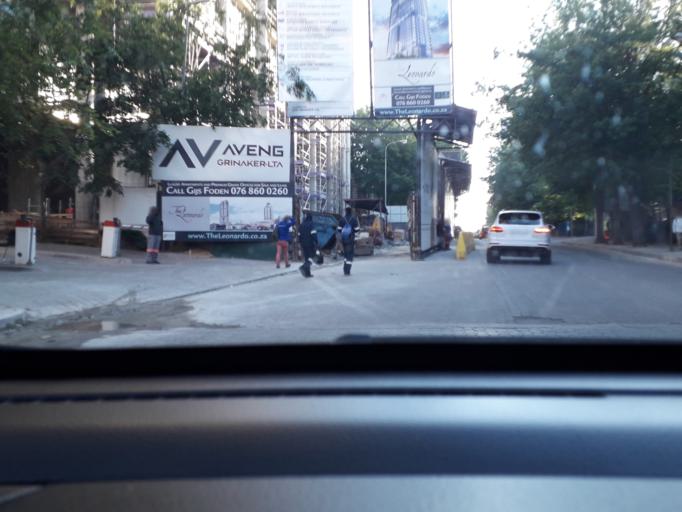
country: ZA
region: Gauteng
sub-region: City of Johannesburg Metropolitan Municipality
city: Johannesburg
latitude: -26.1048
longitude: 28.0552
